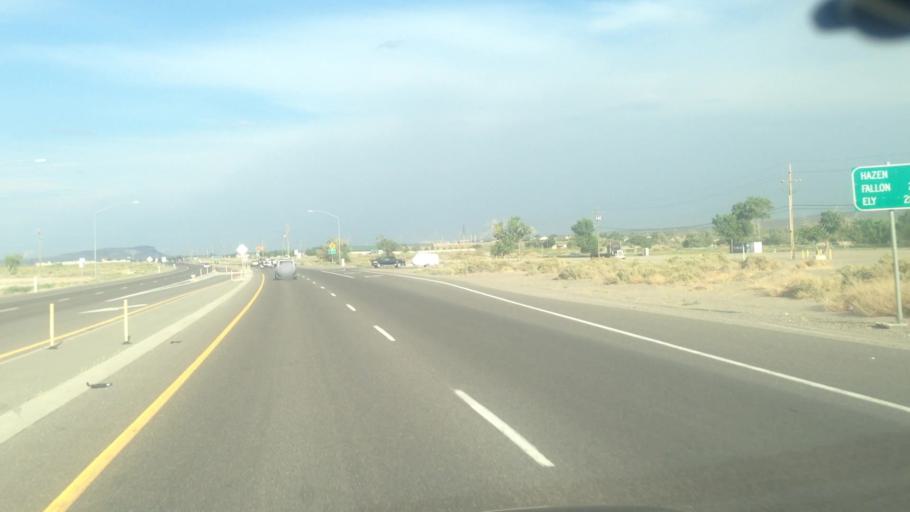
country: US
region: Nevada
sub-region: Lyon County
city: Fernley
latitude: 39.6018
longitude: -119.2214
